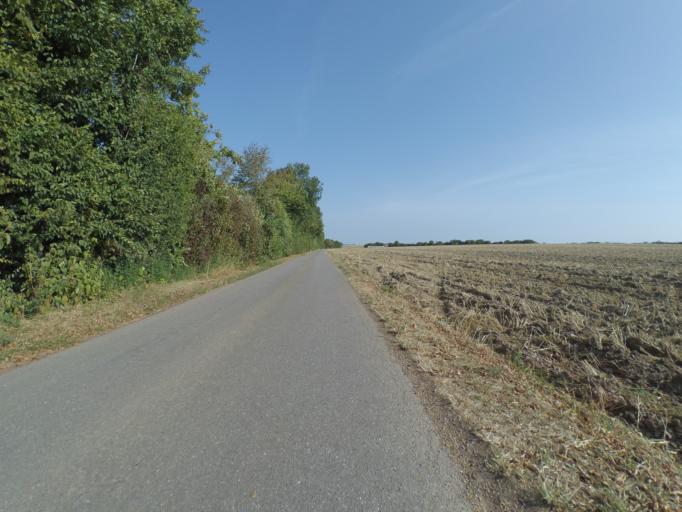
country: DE
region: Rheinland-Pfalz
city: Kirf
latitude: 49.5623
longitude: 6.4780
